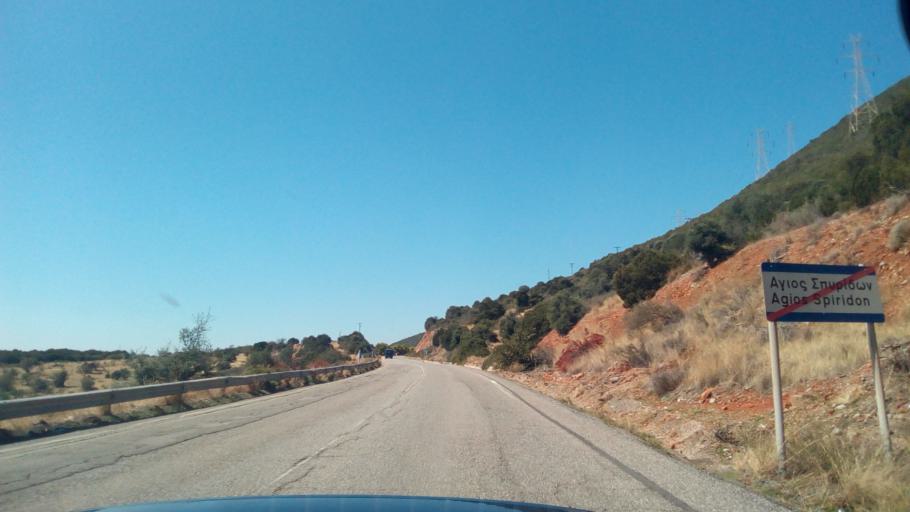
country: GR
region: West Greece
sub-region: Nomos Achaias
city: Selianitika
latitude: 38.3678
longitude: 22.1161
